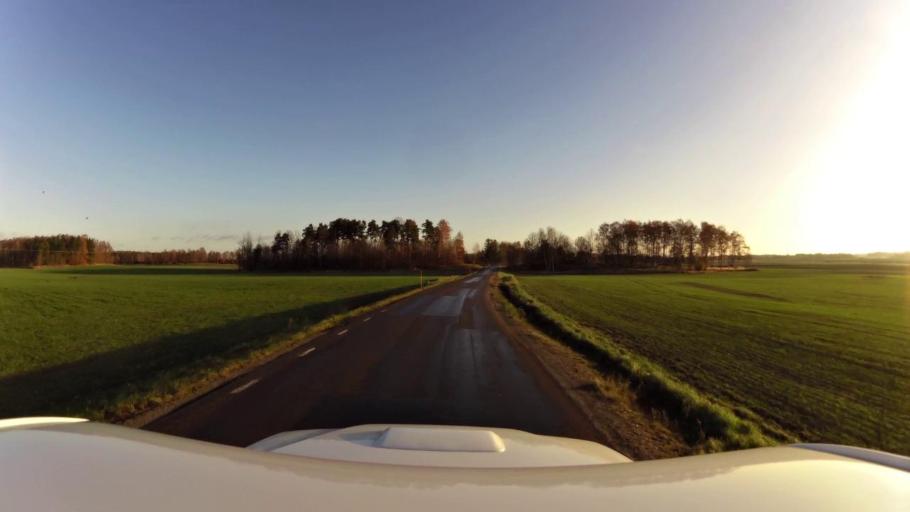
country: SE
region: OEstergoetland
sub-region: Linkopings Kommun
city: Ekangen
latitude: 58.4422
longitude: 15.6787
